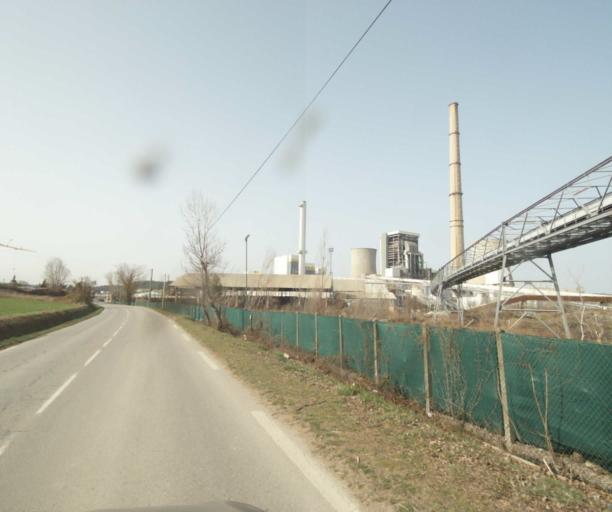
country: FR
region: Provence-Alpes-Cote d'Azur
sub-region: Departement des Bouches-du-Rhone
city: Meyreuil
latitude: 43.4676
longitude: 5.4938
